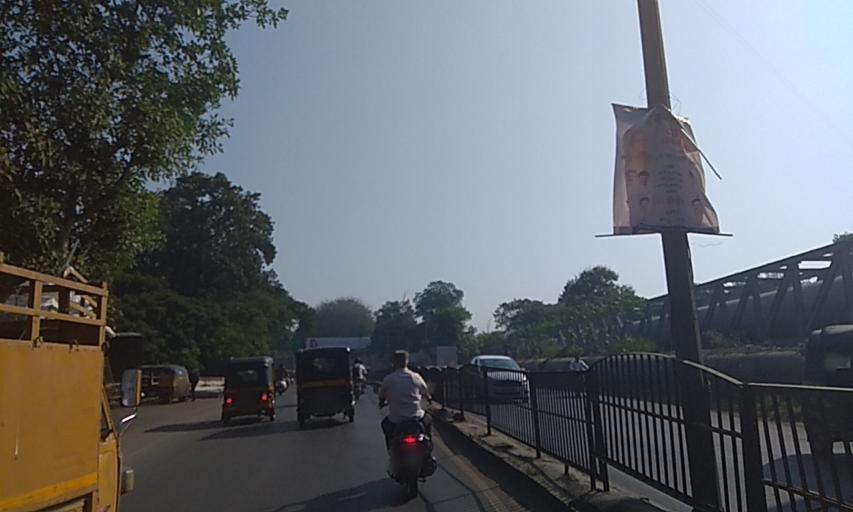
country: IN
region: Maharashtra
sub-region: Pune Division
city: Pune
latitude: 18.4990
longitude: 73.8515
